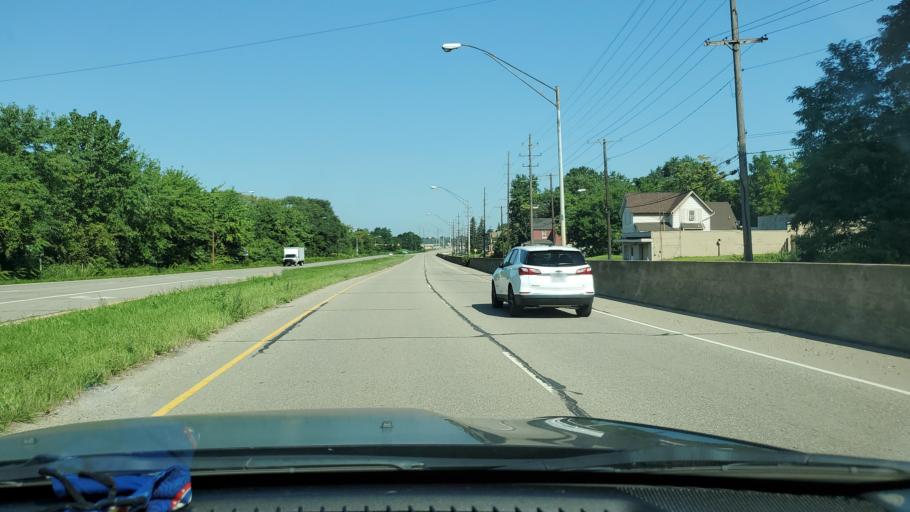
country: US
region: Ohio
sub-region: Trumbull County
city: Girard
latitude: 41.1271
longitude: -80.6804
